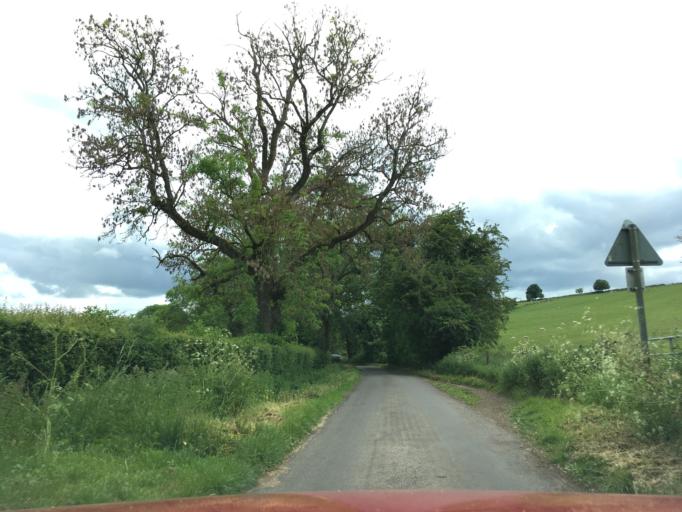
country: GB
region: England
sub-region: Gloucestershire
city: Cirencester
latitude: 51.7568
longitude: -1.9827
